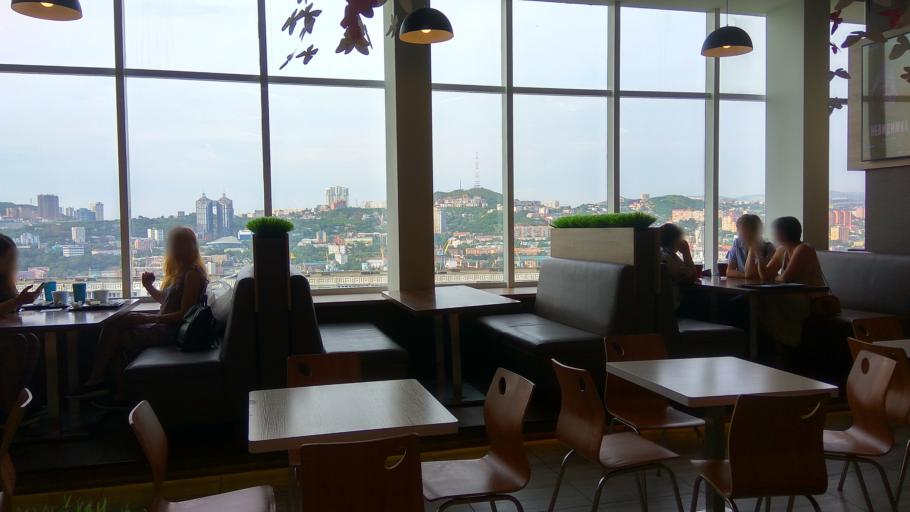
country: RU
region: Primorskiy
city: Vladivostok
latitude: 43.1006
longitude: 131.9032
